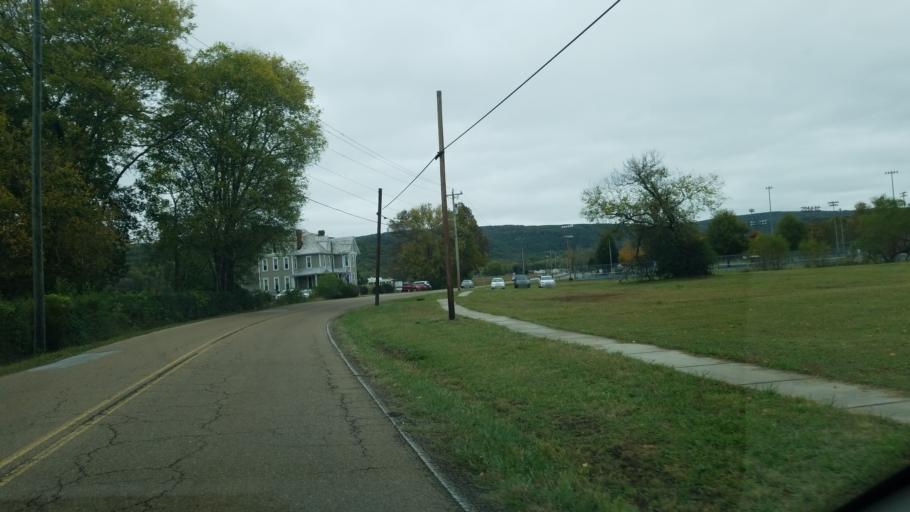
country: US
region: Tennessee
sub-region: Rhea County
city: Dayton
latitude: 35.4915
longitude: -85.0228
